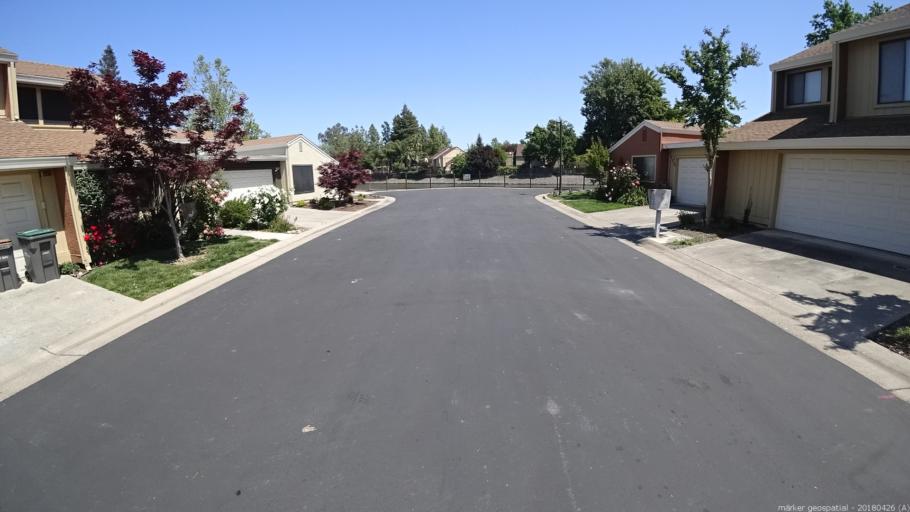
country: US
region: California
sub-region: Yolo County
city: West Sacramento
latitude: 38.5499
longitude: -121.5498
